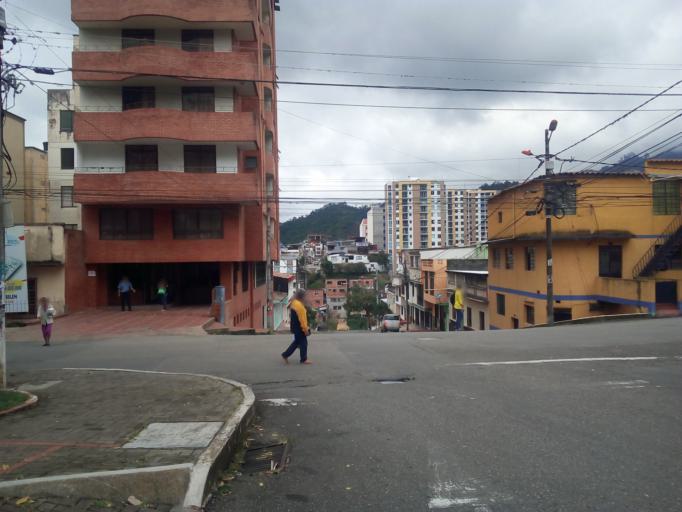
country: CO
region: Tolima
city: Ibague
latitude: 4.4510
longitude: -75.2444
